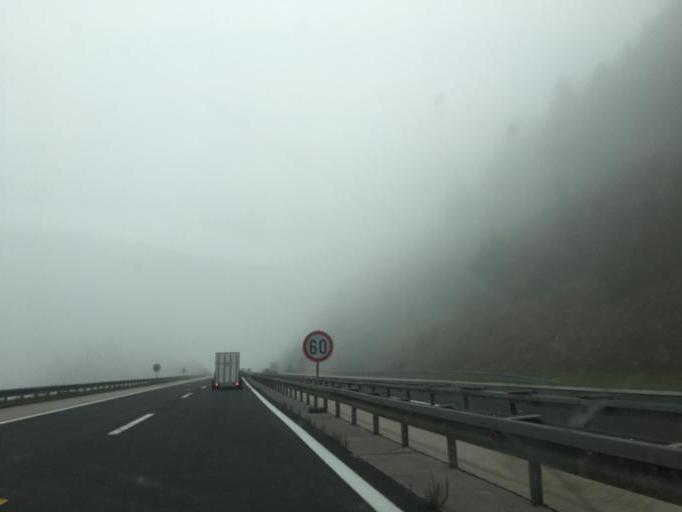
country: HR
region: Licko-Senjska
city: Otocac
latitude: 44.8540
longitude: 15.2254
